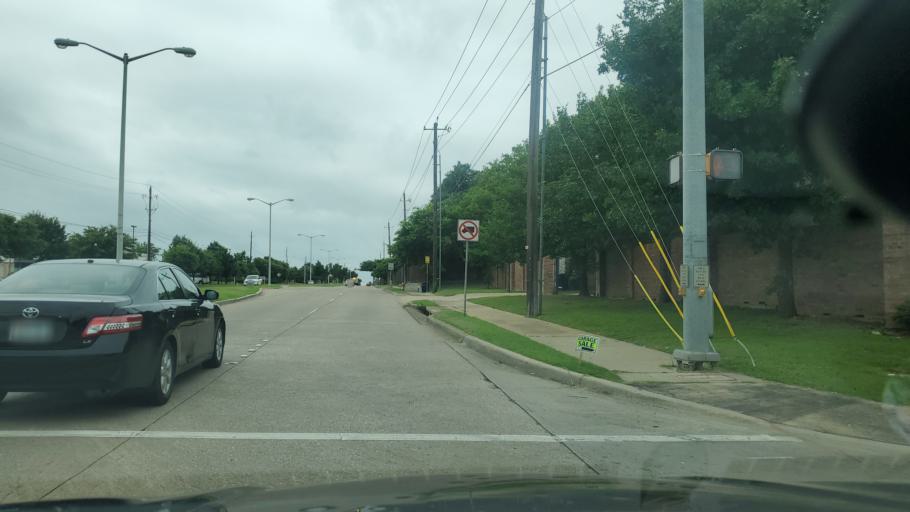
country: US
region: Texas
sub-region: Dallas County
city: Garland
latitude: 32.9515
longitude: -96.6655
